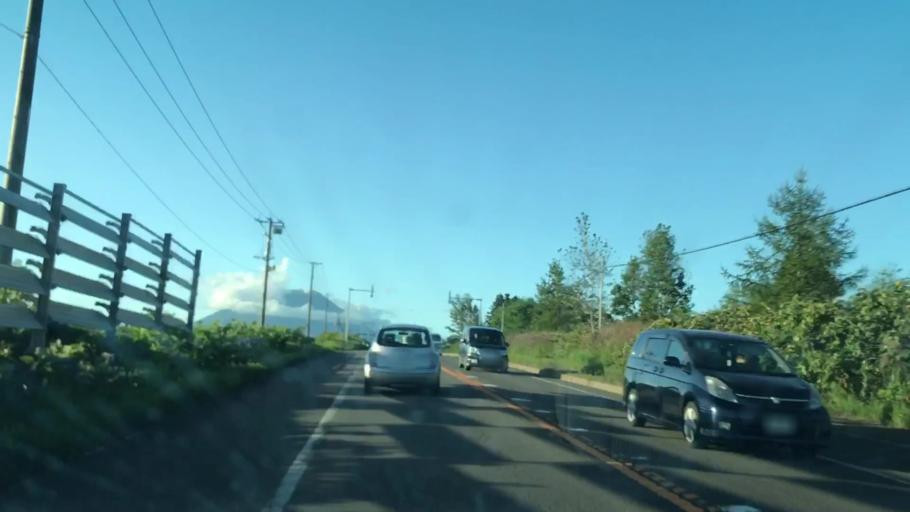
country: JP
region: Hokkaido
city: Date
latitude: 42.6699
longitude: 140.8425
